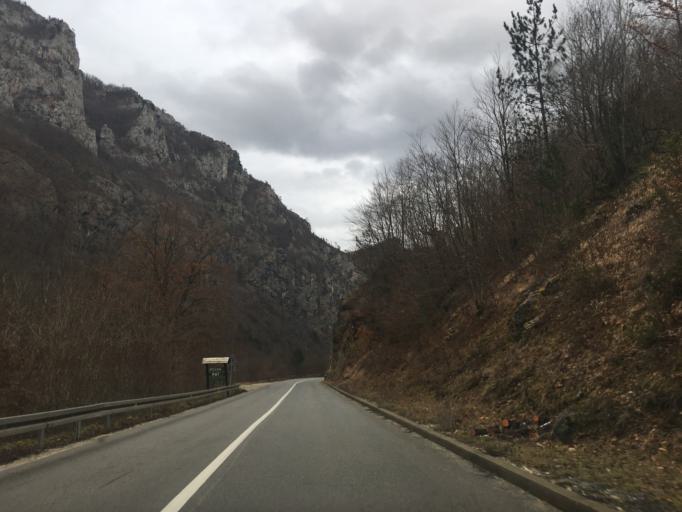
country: RS
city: Sokolovo Brdo
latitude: 43.1817
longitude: 19.7635
